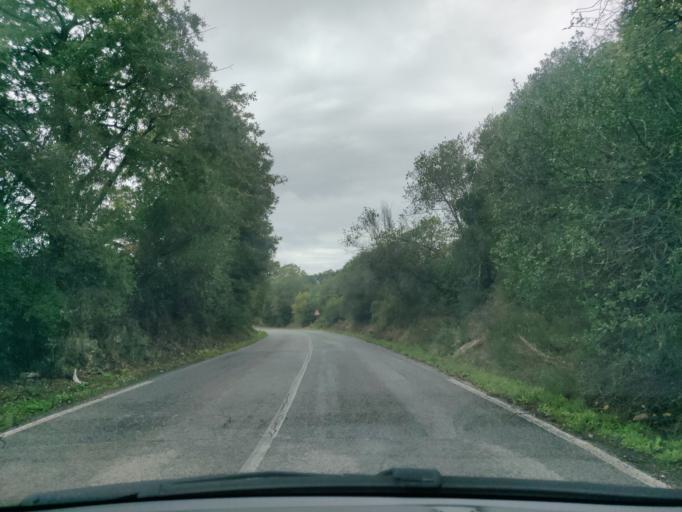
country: IT
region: Latium
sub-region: Citta metropolitana di Roma Capitale
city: Allumiere
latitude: 42.1351
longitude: 11.8702
